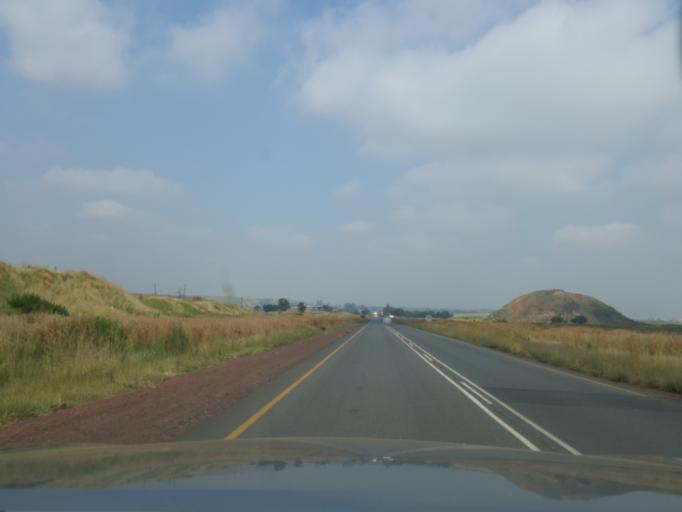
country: ZA
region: Mpumalanga
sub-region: Nkangala District Municipality
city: Witbank
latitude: -26.0144
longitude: 29.3867
